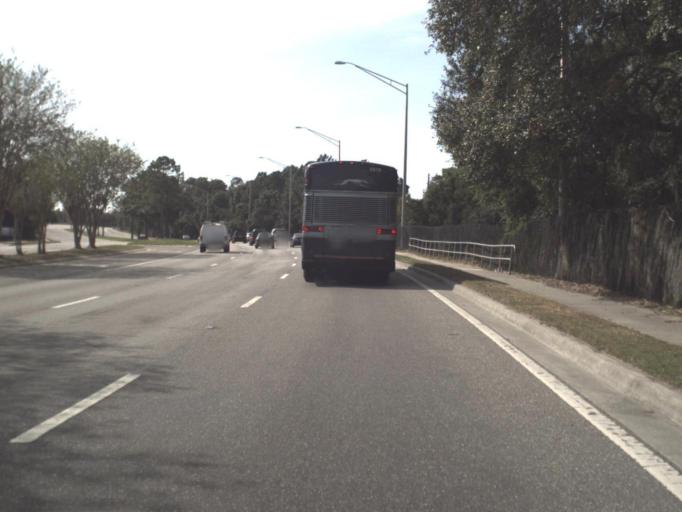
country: US
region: Florida
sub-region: Orange County
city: Orlando
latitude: 28.5251
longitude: -81.4172
